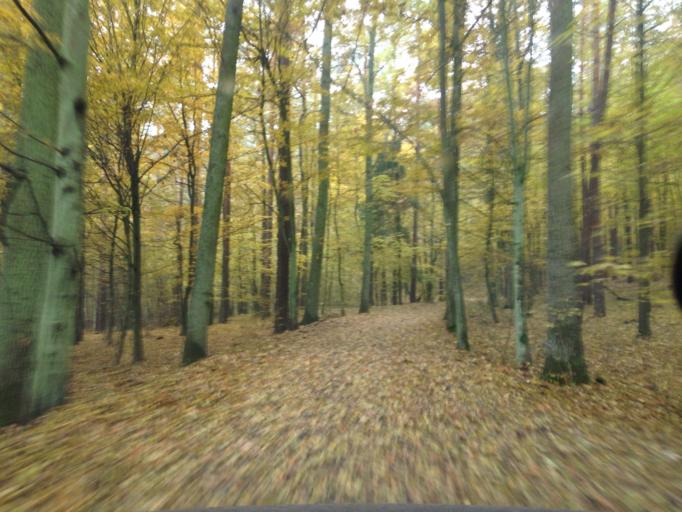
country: PL
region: Kujawsko-Pomorskie
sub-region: Powiat brodnicki
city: Gorzno
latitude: 53.2266
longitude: 19.7162
